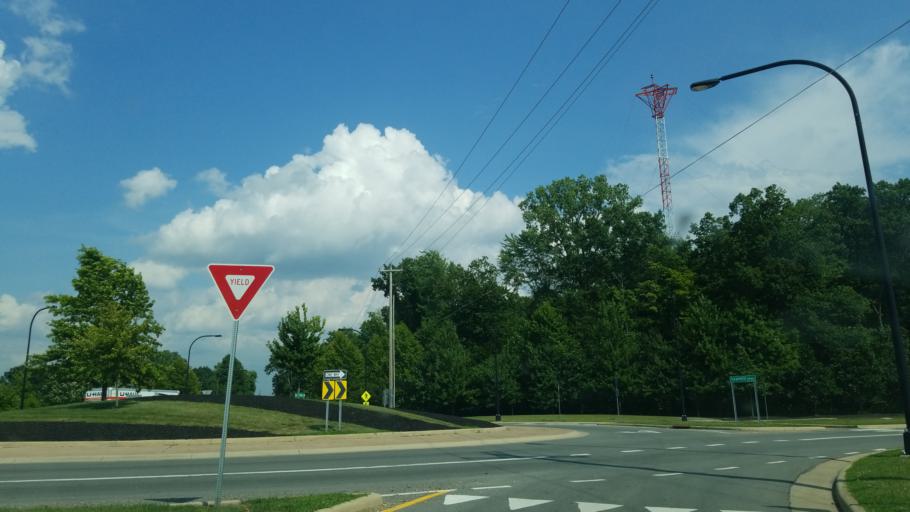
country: US
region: Ohio
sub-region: Delaware County
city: Powell
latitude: 40.2164
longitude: -83.0972
